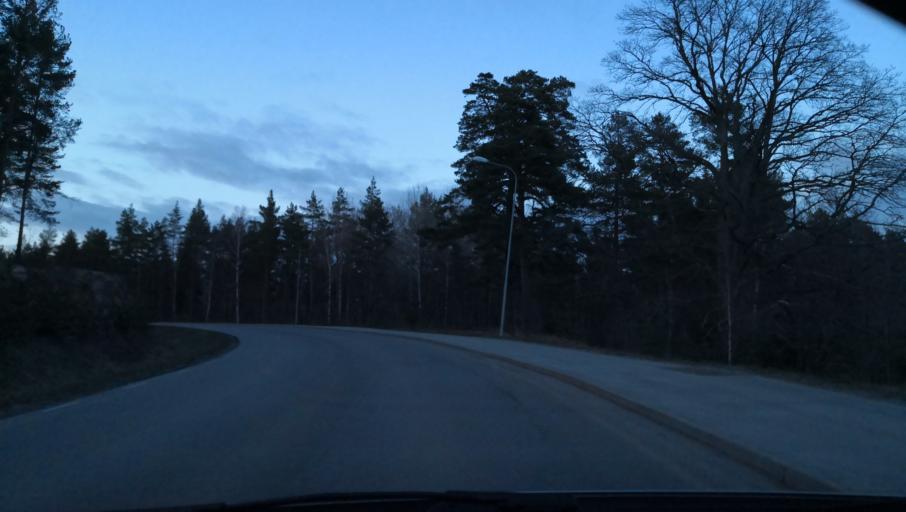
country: SE
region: Stockholm
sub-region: Nacka Kommun
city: Boo
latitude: 59.3396
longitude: 18.2977
